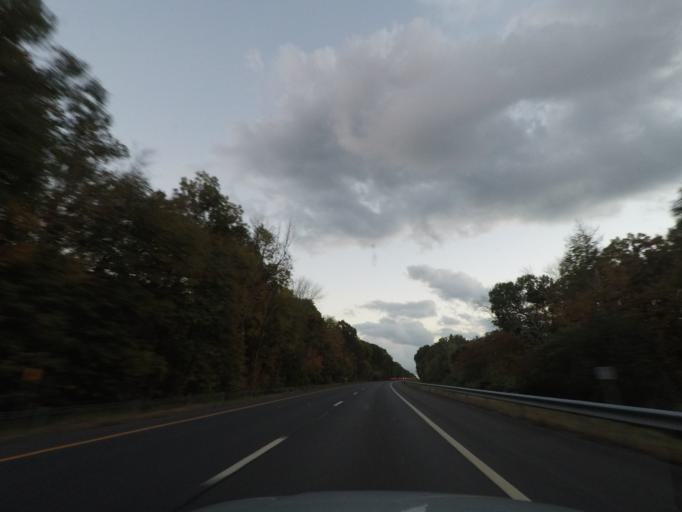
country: US
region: New York
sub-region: Ulster County
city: Tillson
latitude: 41.7866
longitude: -74.0505
